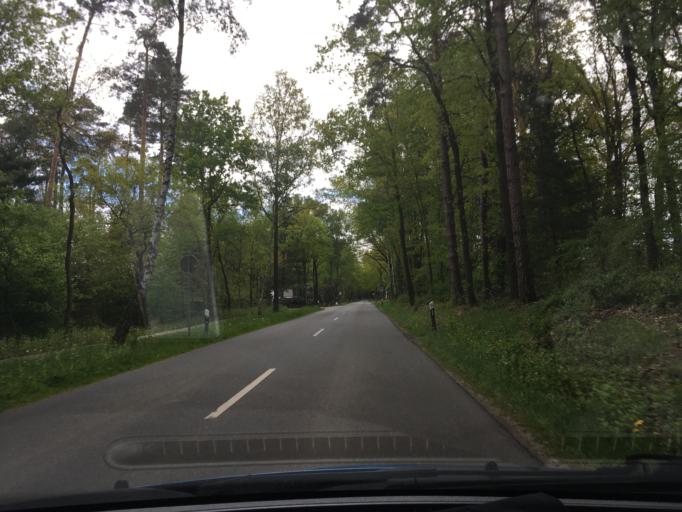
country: DE
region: Lower Saxony
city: Suderburg
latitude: 52.8662
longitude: 10.4277
